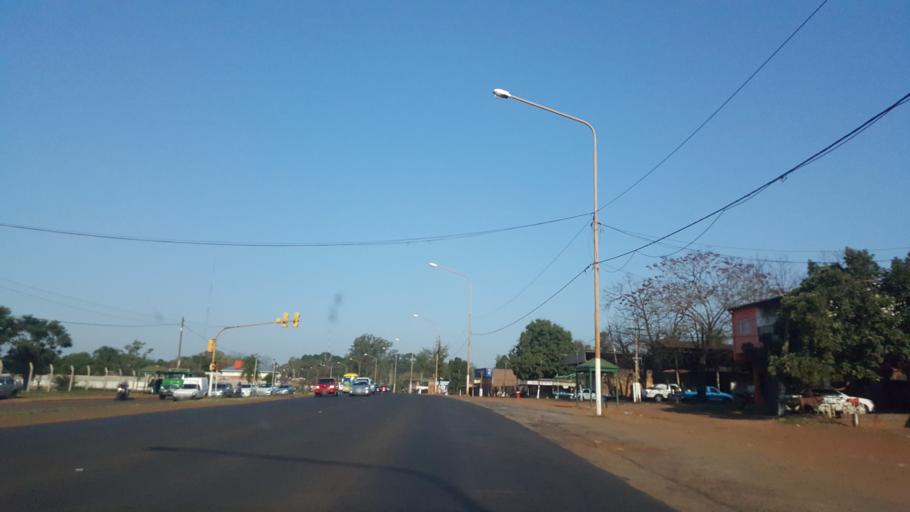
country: AR
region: Misiones
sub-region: Departamento de Capital
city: Posadas
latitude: -27.4233
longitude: -55.8979
